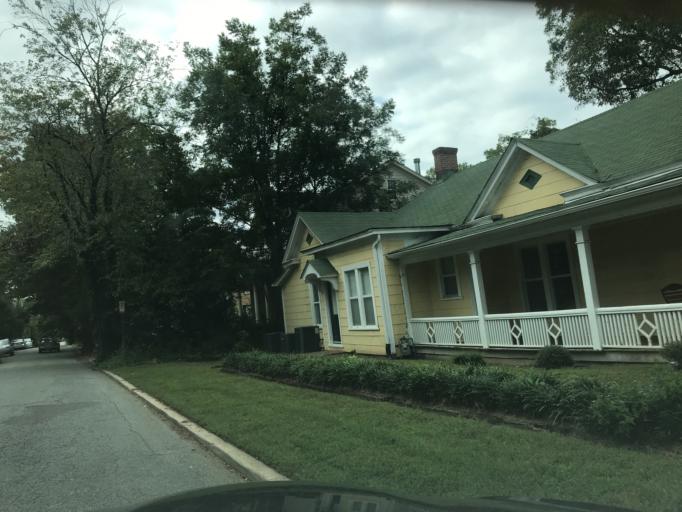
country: US
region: North Carolina
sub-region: Orange County
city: Chapel Hill
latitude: 35.9163
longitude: -79.0541
